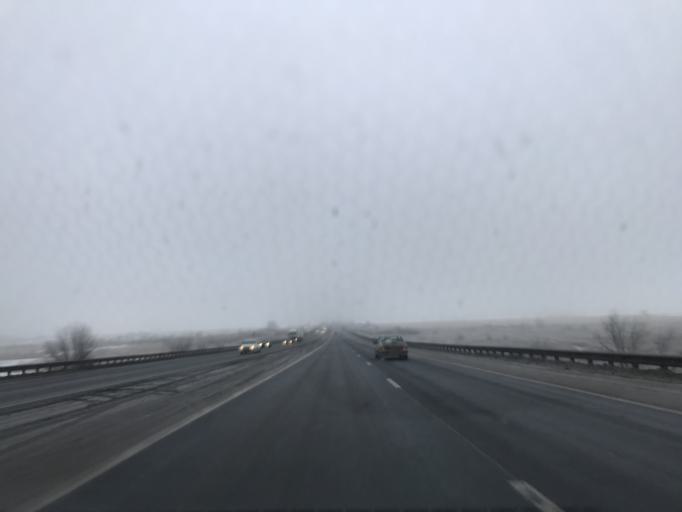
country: RU
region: Rostov
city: Grushevskaya
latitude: 47.4409
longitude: 39.9747
